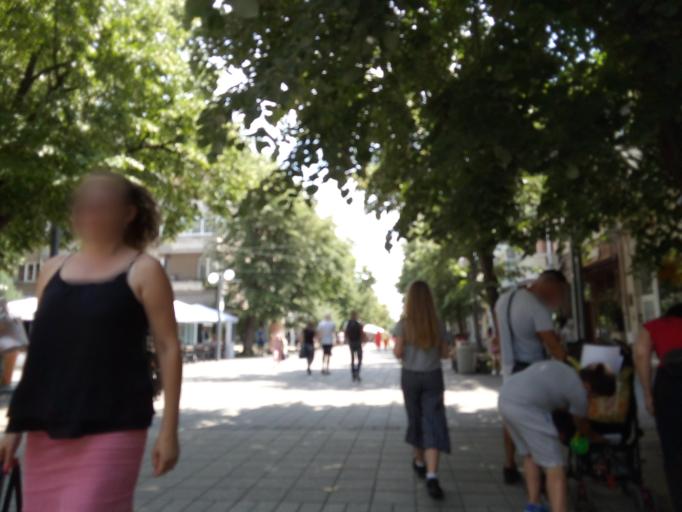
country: BG
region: Burgas
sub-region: Obshtina Burgas
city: Burgas
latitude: 42.4951
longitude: 27.4718
